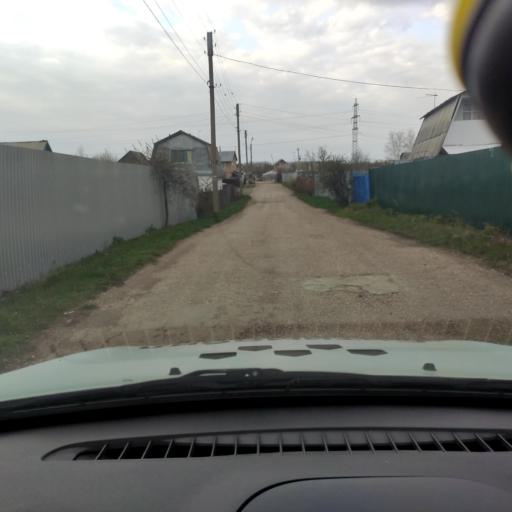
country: RU
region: Samara
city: Mezhdurechensk
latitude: 53.2472
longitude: 49.1479
